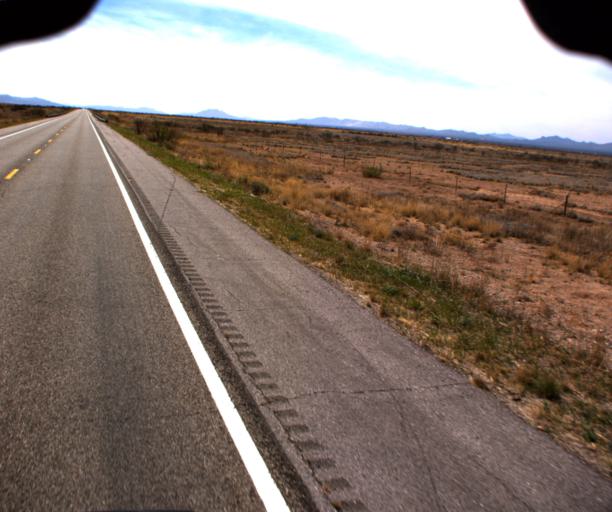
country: US
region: Arizona
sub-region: Cochise County
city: Pirtleville
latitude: 31.5305
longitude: -109.6514
